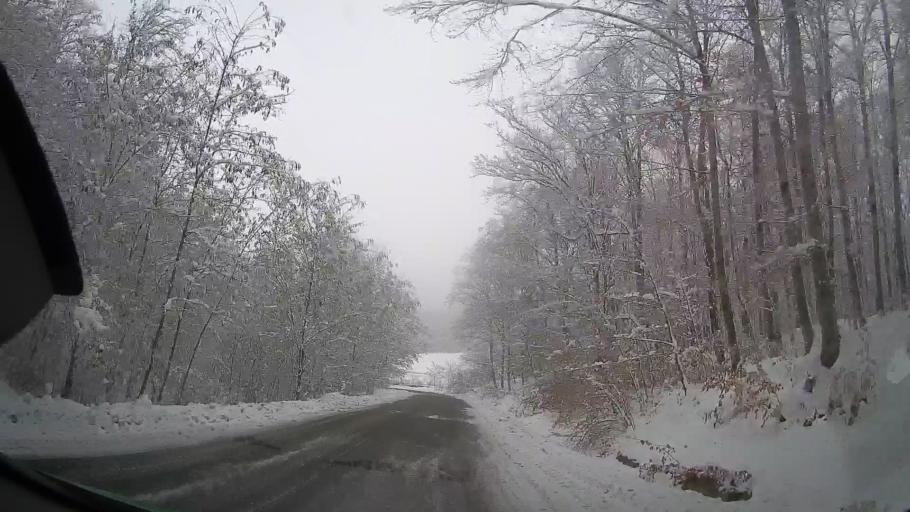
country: RO
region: Neamt
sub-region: Comuna Valea Ursului
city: Valea Ursului
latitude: 46.8485
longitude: 27.0646
